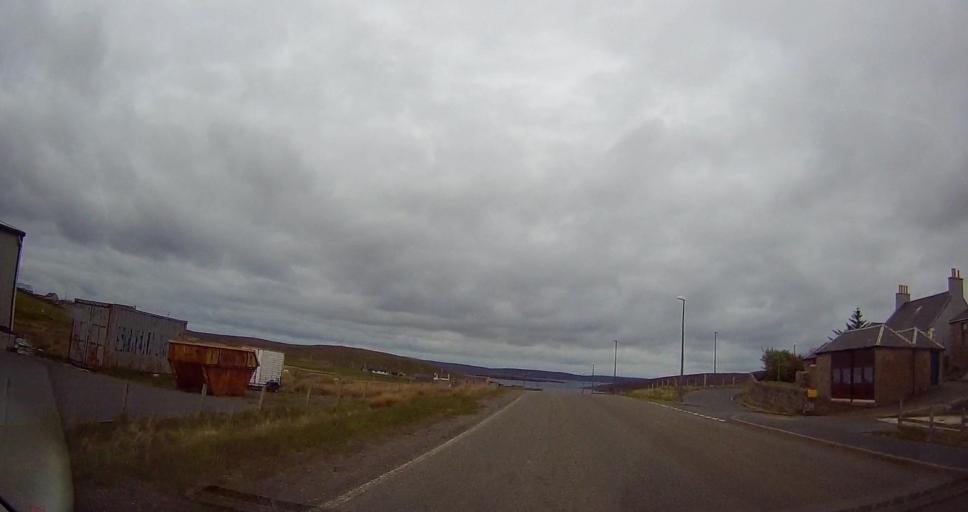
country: GB
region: Scotland
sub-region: Shetland Islands
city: Shetland
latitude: 60.5992
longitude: -1.0769
